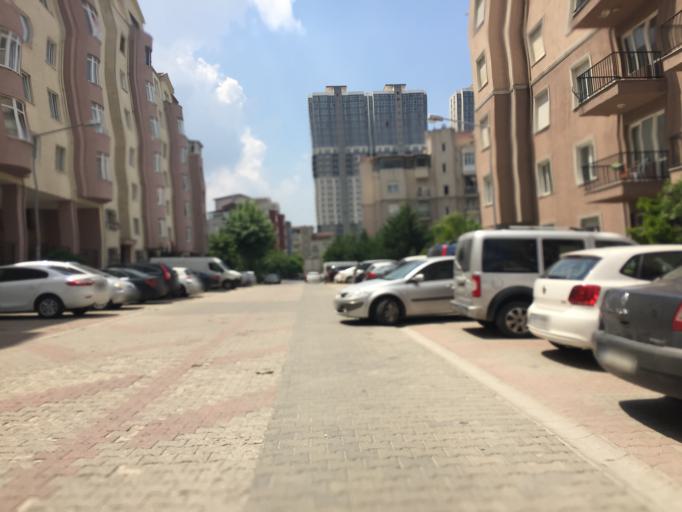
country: TR
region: Istanbul
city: Esenyurt
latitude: 41.0730
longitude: 28.6644
